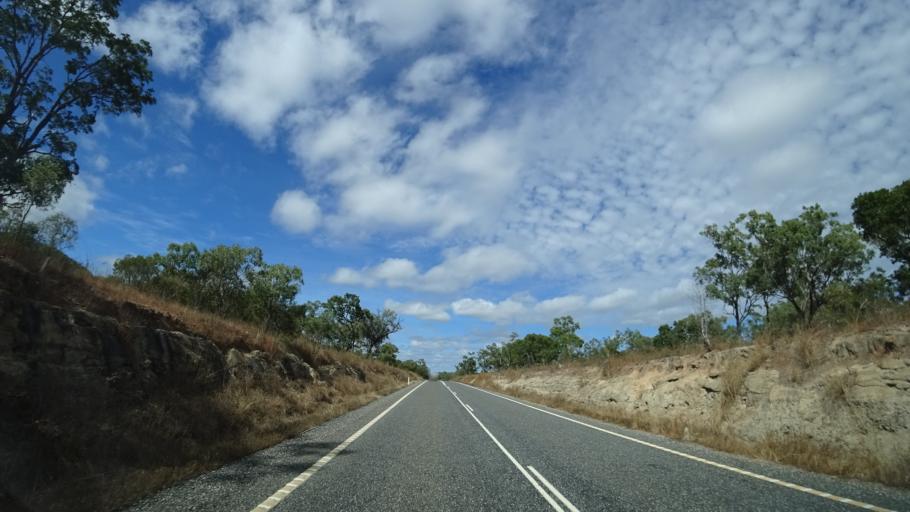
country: AU
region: Queensland
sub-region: Cairns
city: Port Douglas
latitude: -16.3273
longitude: 144.7208
